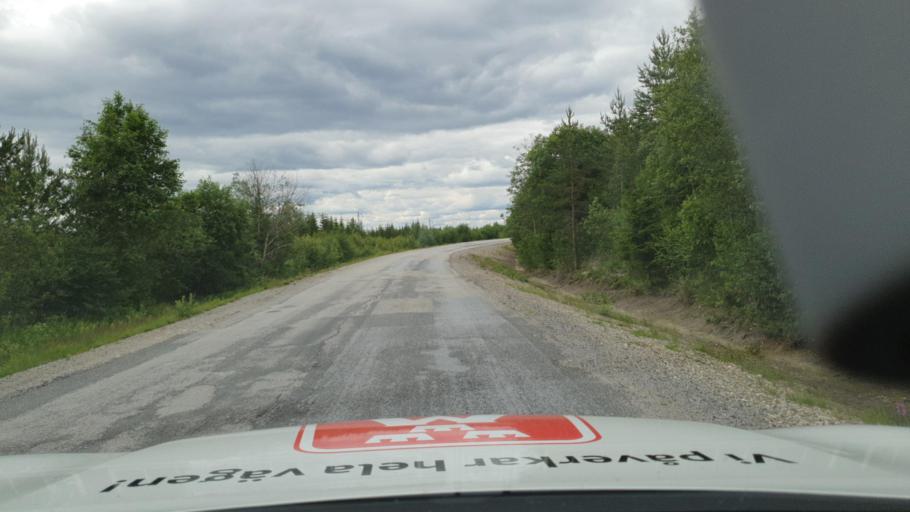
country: SE
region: Vaesterbotten
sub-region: Bjurholms Kommun
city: Bjurholm
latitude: 63.7694
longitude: 19.2503
